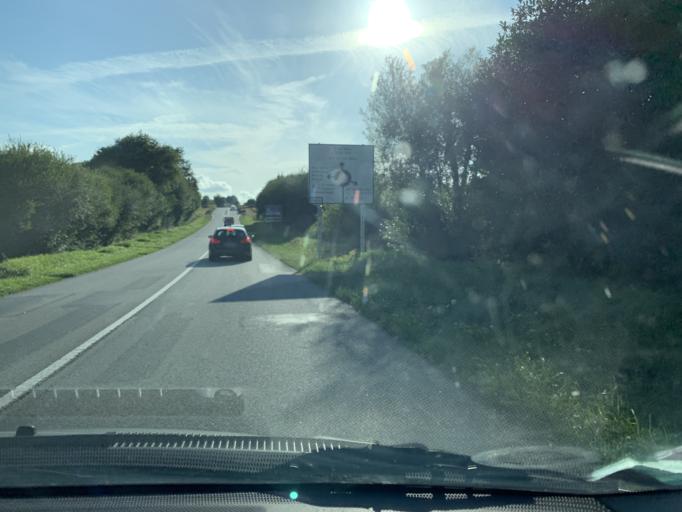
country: FR
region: Brittany
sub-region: Departement du Morbihan
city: Surzur
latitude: 47.5767
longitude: -2.6243
